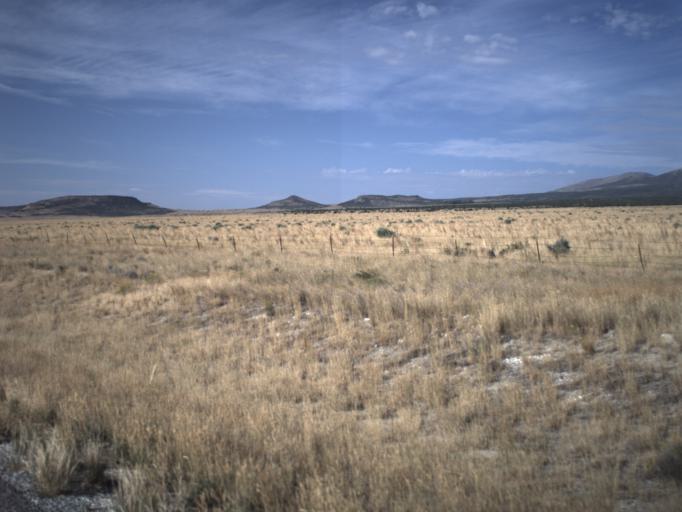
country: US
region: Idaho
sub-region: Oneida County
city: Malad City
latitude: 41.8912
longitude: -113.1117
